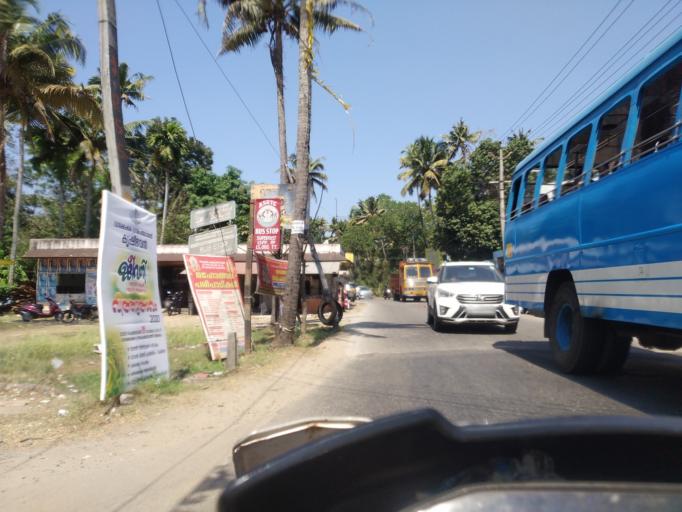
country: IN
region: Kerala
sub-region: Thrissur District
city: Kodungallur
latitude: 10.1675
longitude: 76.2130
